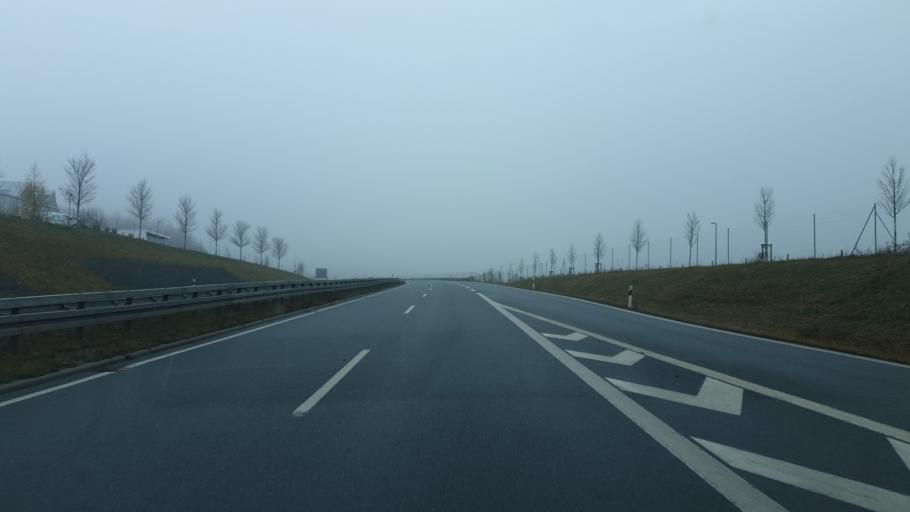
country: DE
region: Saxony
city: Gornau
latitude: 50.7880
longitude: 12.9959
